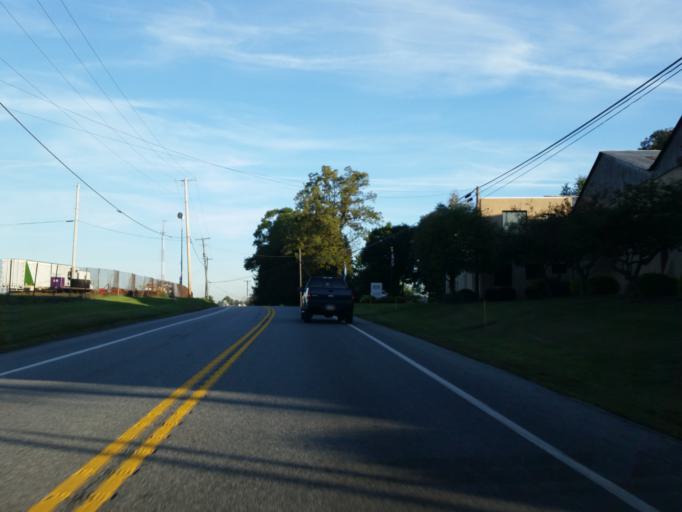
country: US
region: Pennsylvania
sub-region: Lancaster County
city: Quarryville
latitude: 39.8816
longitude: -76.2315
